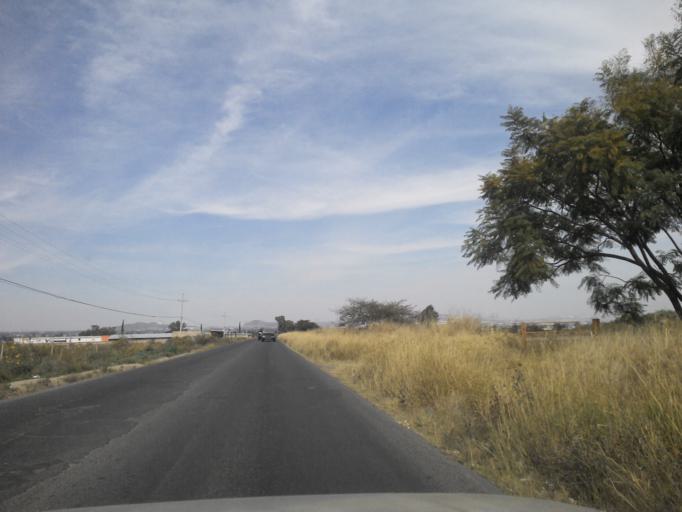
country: MX
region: Jalisco
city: San Sebastian el Grande
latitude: 20.5077
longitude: -103.4136
